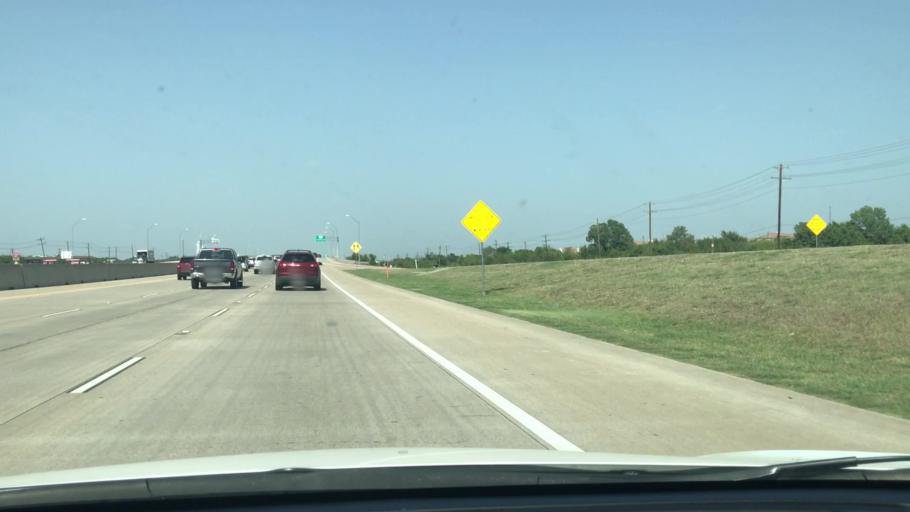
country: US
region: Texas
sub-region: Collin County
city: Frisco
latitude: 33.1170
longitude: -96.7555
